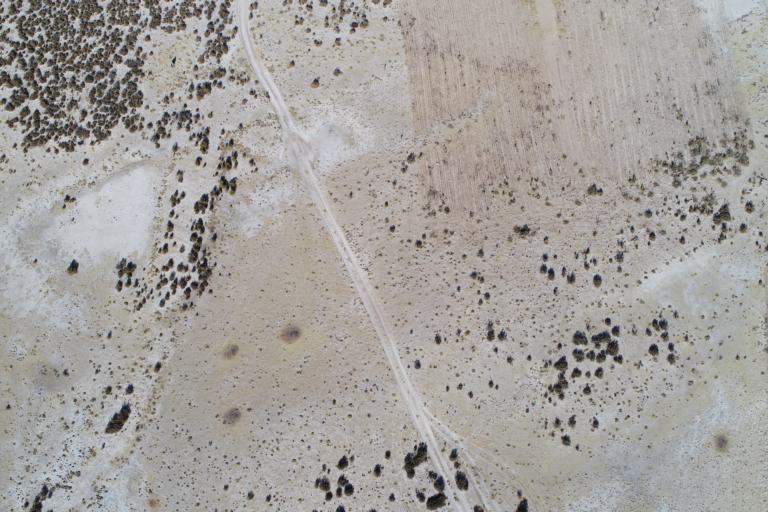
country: BO
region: Potosi
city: Colchani
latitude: -20.3495
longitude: -66.8840
